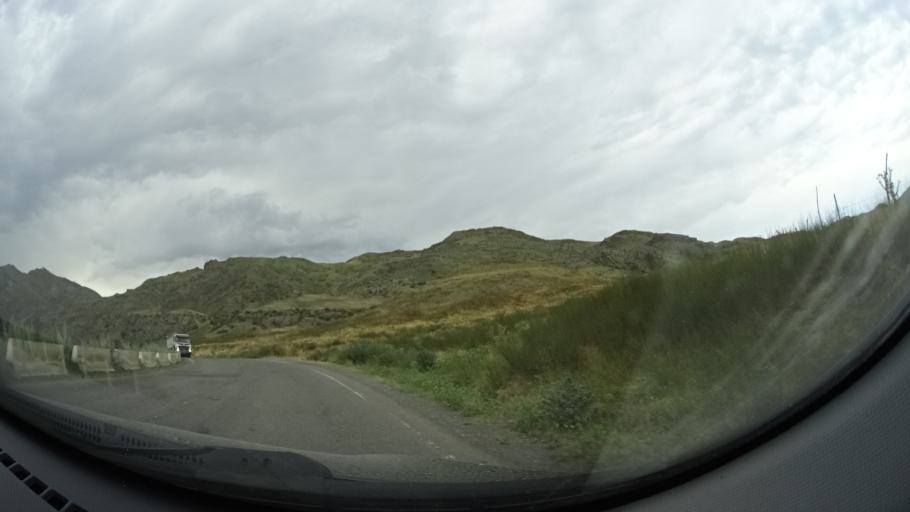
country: GE
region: Samtskhe-Javakheti
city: Akhaltsikhe
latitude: 41.6164
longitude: 43.1156
